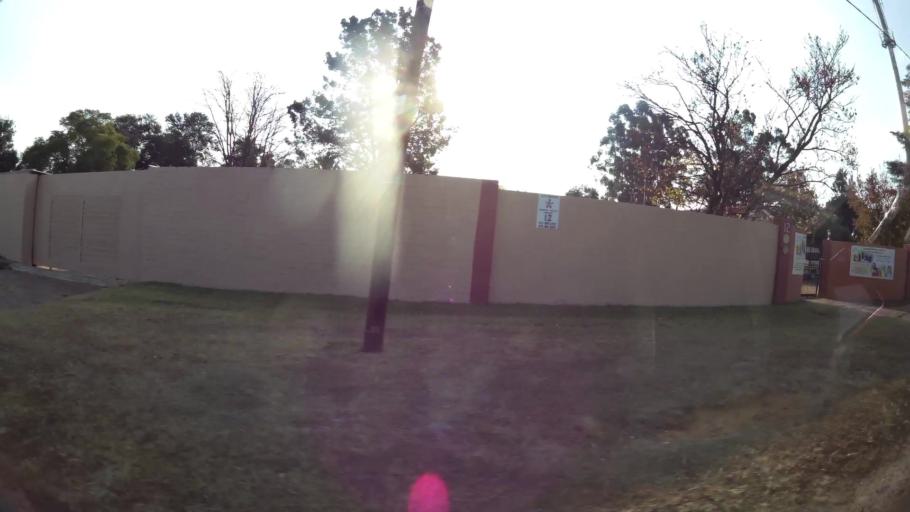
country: ZA
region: Gauteng
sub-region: Ekurhuleni Metropolitan Municipality
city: Benoni
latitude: -26.1433
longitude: 28.3619
